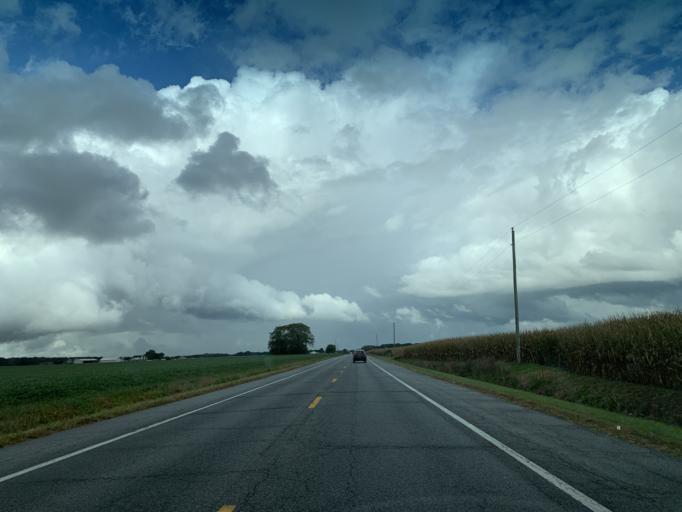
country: US
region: Maryland
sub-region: Caroline County
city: Greensboro
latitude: 39.1202
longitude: -75.8686
